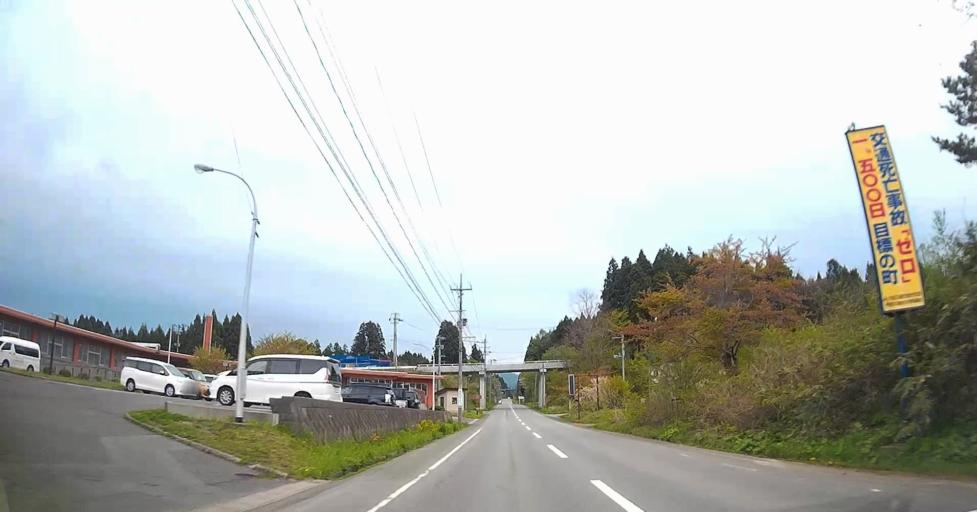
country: JP
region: Aomori
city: Goshogawara
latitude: 41.1778
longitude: 140.4789
